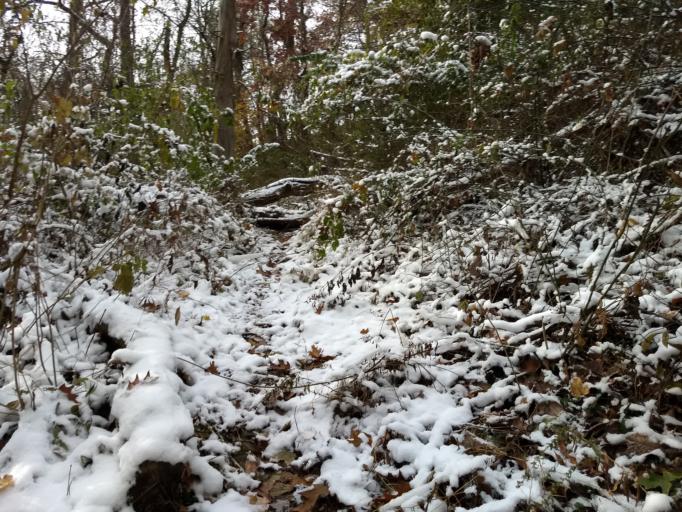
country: US
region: Pennsylvania
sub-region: Allegheny County
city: Mount Oliver
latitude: 40.4060
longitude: -80.0083
